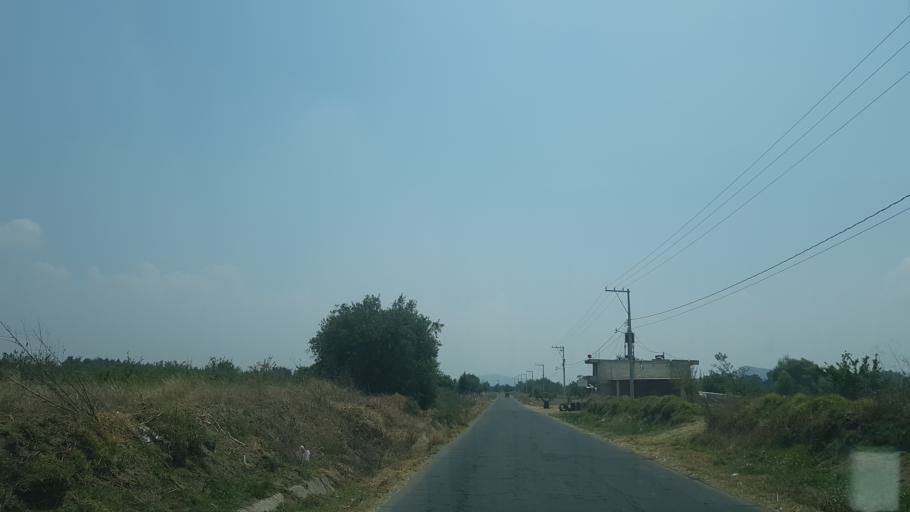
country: MX
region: Puebla
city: San Andres Calpan
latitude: 19.1008
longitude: -98.4397
